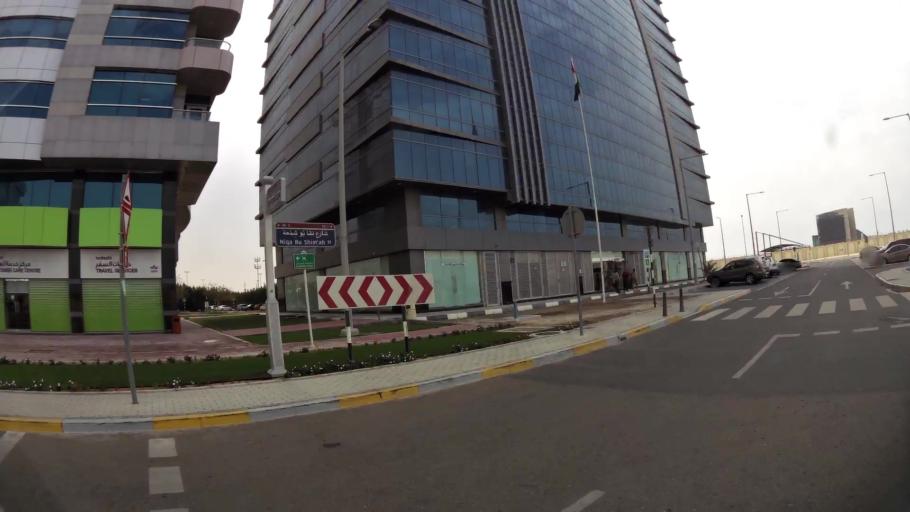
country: AE
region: Abu Dhabi
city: Abu Dhabi
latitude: 24.4284
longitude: 54.4632
